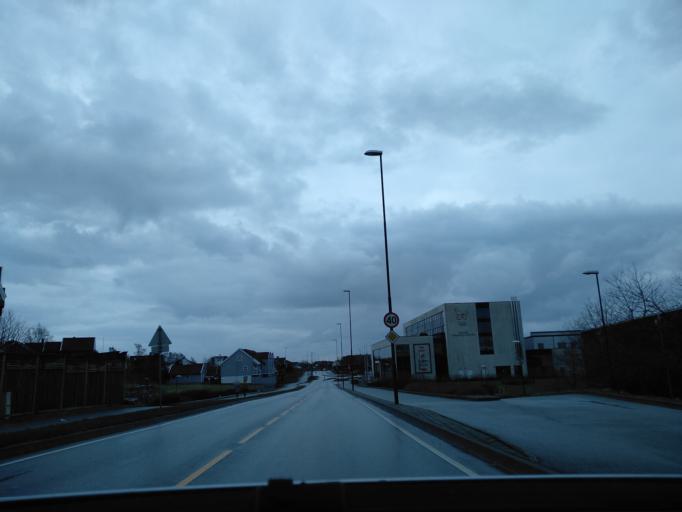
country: NO
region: Rogaland
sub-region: Stavanger
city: Stavanger
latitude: 58.9856
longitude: 5.6932
